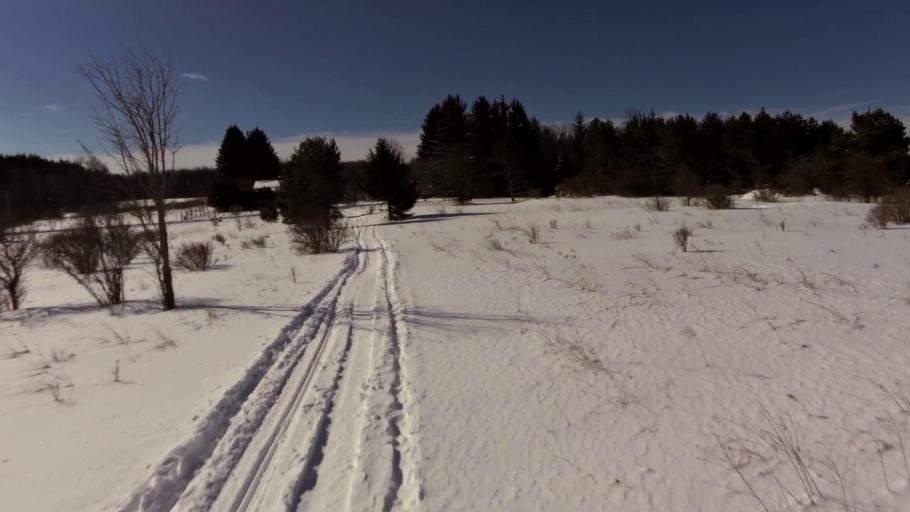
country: US
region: New York
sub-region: Cattaraugus County
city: Franklinville
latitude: 42.3437
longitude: -78.3767
